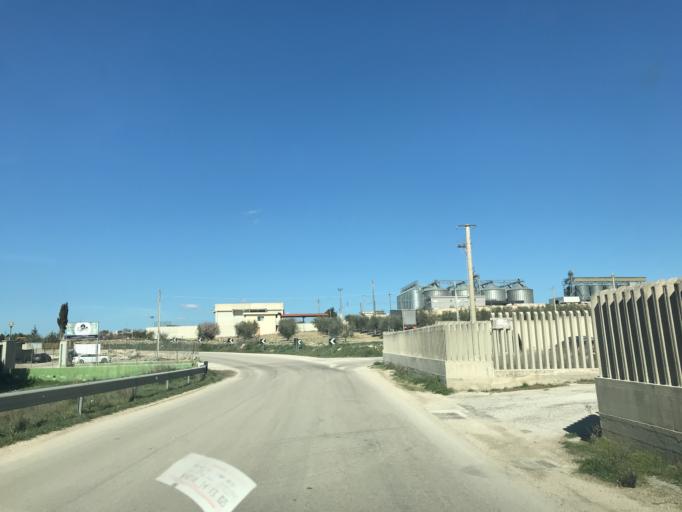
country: IT
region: Apulia
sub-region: Provincia di Bari
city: Gravina in Puglia
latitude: 40.8396
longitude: 16.4275
